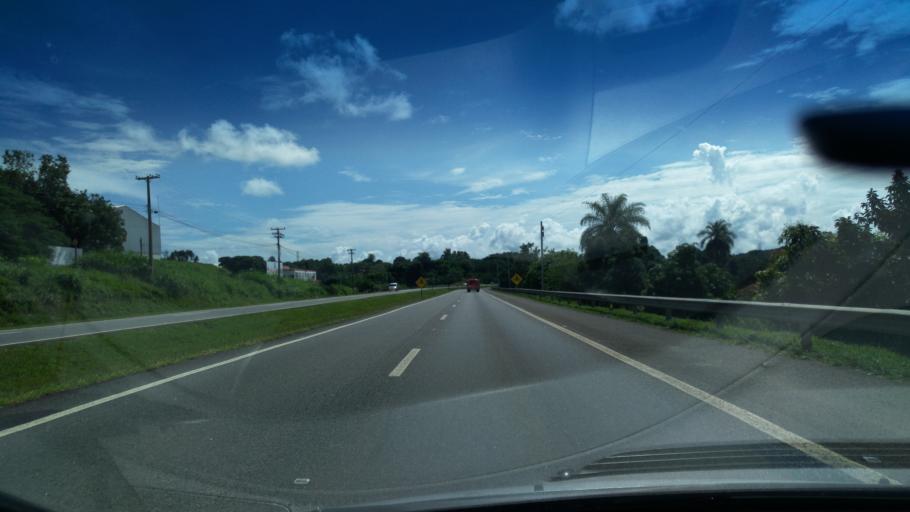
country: BR
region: Sao Paulo
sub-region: Santo Antonio Do Jardim
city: Espirito Santo do Pinhal
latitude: -22.2029
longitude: -46.7777
